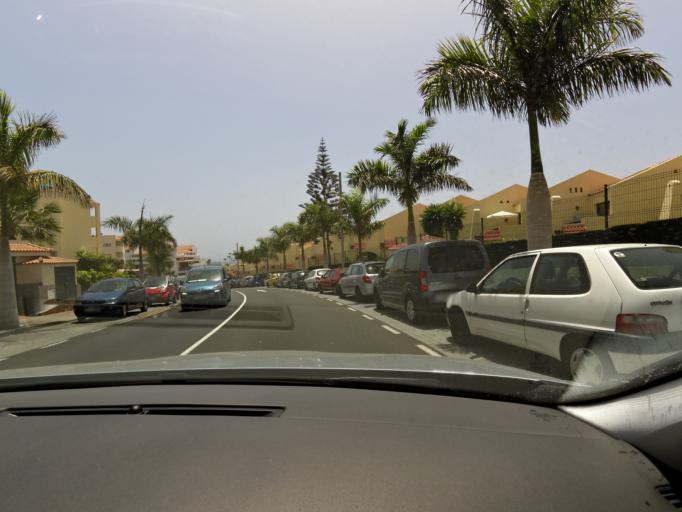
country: ES
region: Canary Islands
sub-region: Provincia de Santa Cruz de Tenerife
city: Playa de las Americas
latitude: 28.0863
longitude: -16.7311
